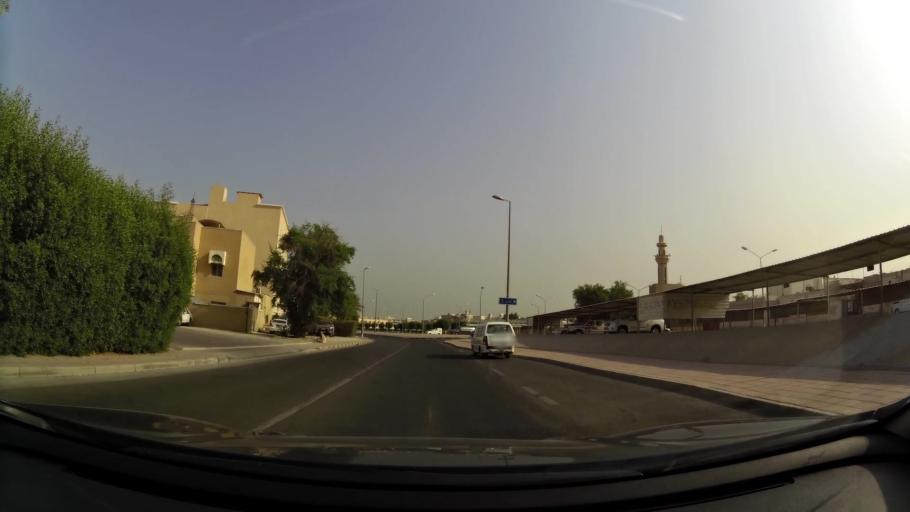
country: KW
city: Al Funaytis
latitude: 29.2161
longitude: 48.0806
